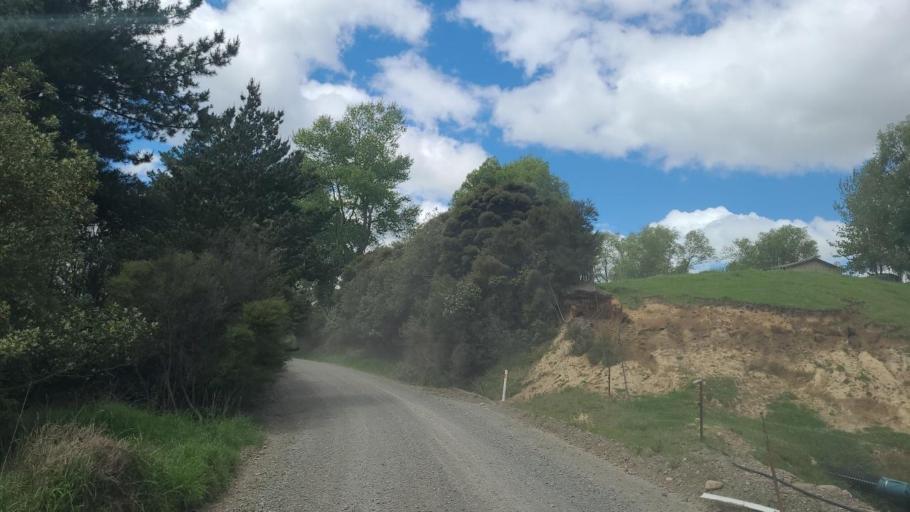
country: NZ
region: Hawke's Bay
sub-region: Napier City
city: Napier
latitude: -39.2206
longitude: 176.7715
